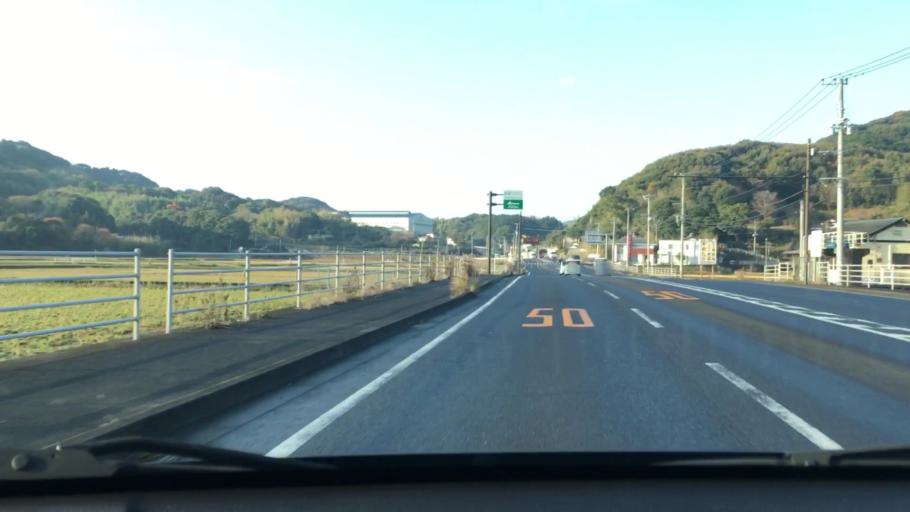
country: JP
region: Nagasaki
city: Sasebo
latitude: 33.1074
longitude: 129.7827
